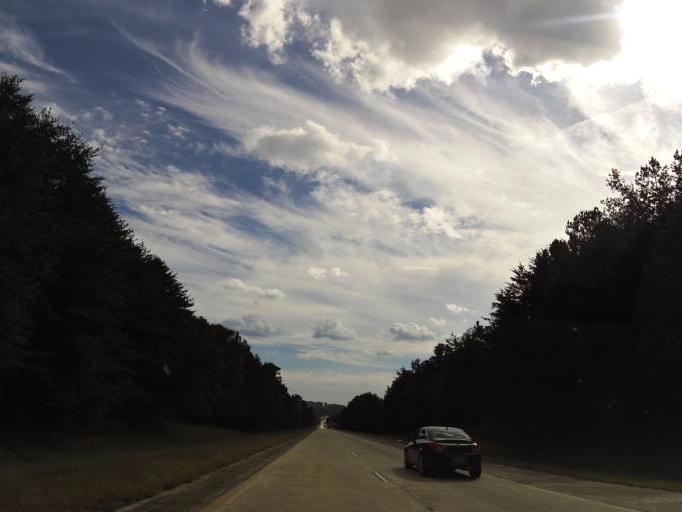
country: US
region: Georgia
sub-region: Cherokee County
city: Ball Ground
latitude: 34.3538
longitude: -84.3917
